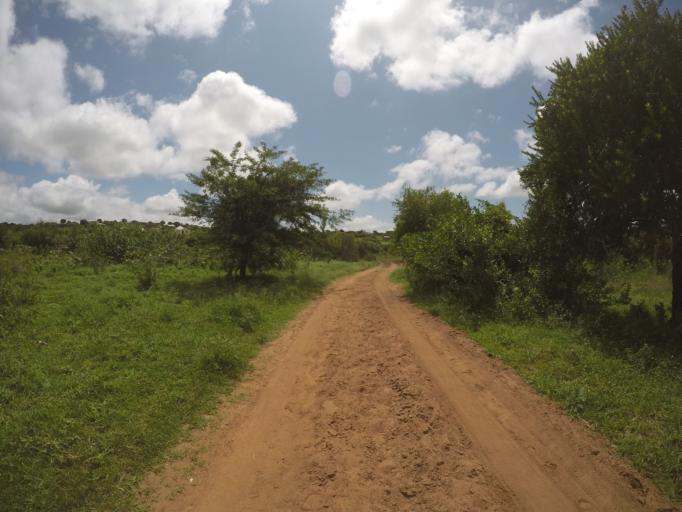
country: ZA
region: KwaZulu-Natal
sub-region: uThungulu District Municipality
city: Empangeni
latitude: -28.5810
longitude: 31.8363
